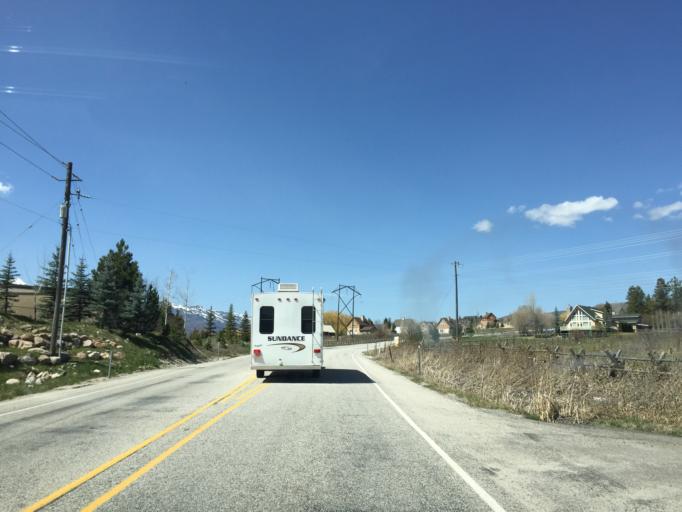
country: US
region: Utah
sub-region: Weber County
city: Wolf Creek
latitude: 41.3197
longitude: -111.8287
